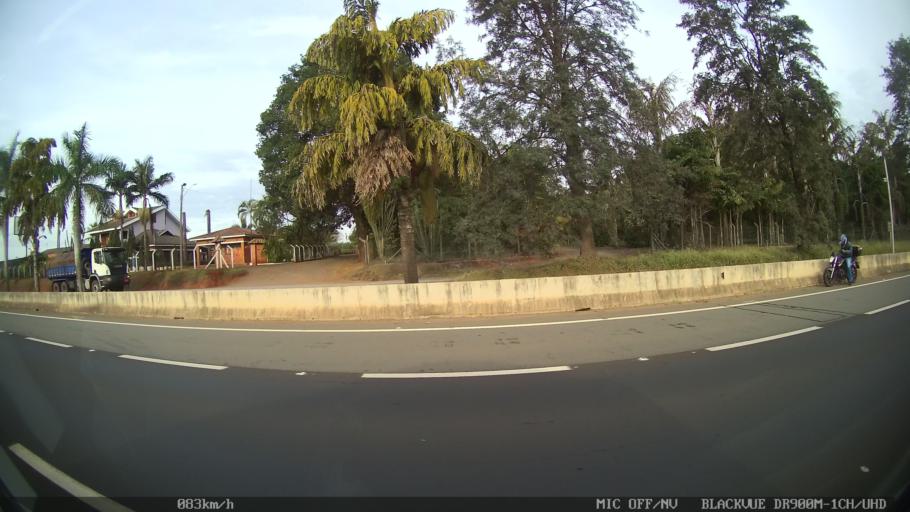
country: BR
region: Sao Paulo
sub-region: Limeira
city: Limeira
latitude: -22.5819
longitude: -47.4542
